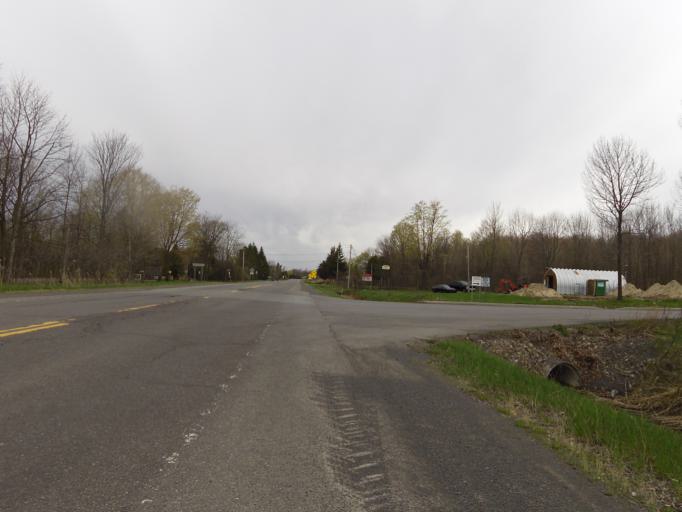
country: CA
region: Quebec
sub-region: Monteregie
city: Hudson
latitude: 45.5284
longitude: -74.2132
